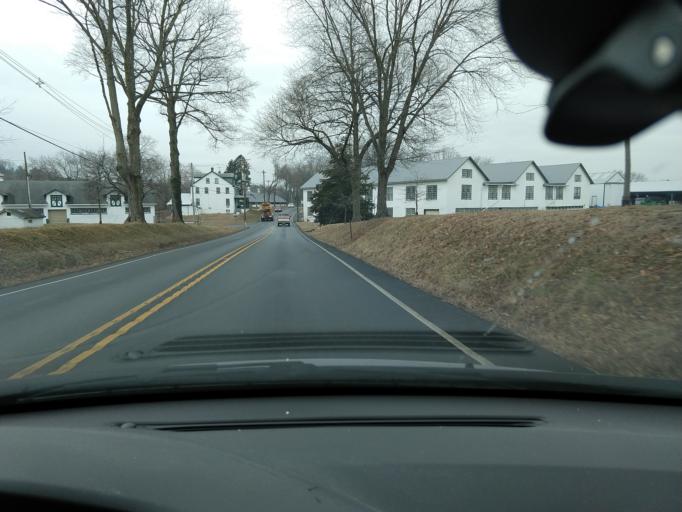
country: US
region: Pennsylvania
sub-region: Montgomery County
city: Stowe
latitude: 40.2346
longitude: -75.6754
